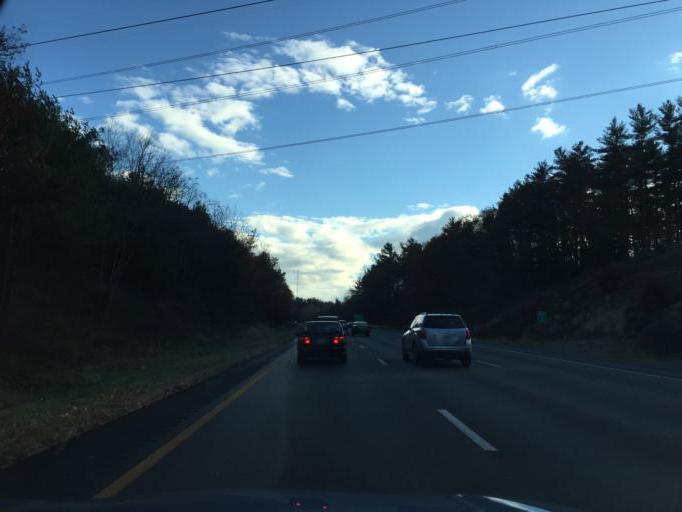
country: US
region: Massachusetts
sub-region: Norfolk County
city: Walpole
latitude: 42.1109
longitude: -71.2318
